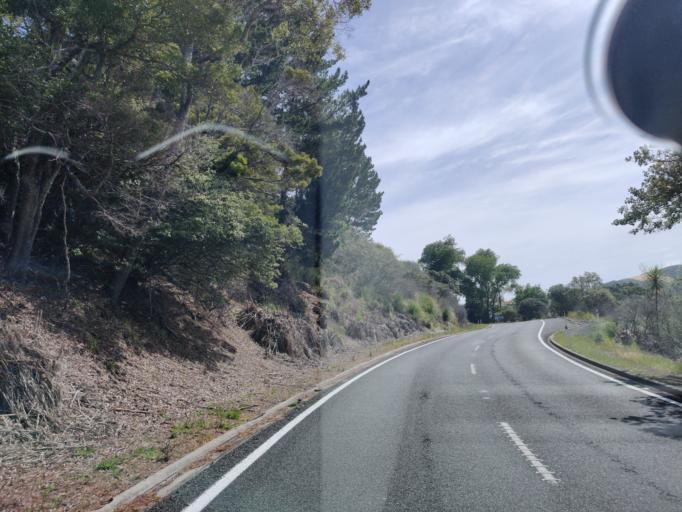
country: NZ
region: Northland
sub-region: Far North District
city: Ahipara
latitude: -35.5018
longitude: 173.4012
